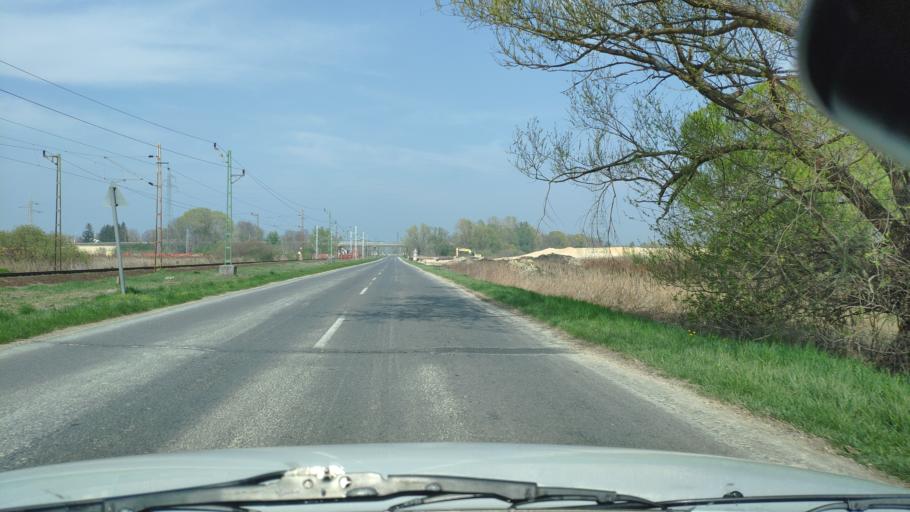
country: HU
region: Somogy
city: Balatonbereny
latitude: 46.6866
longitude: 17.2831
